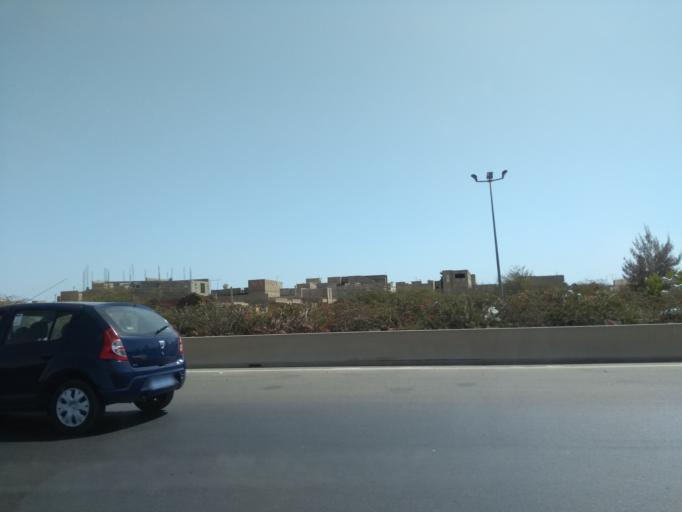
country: SN
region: Dakar
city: Pikine
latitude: 14.7446
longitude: -17.2812
